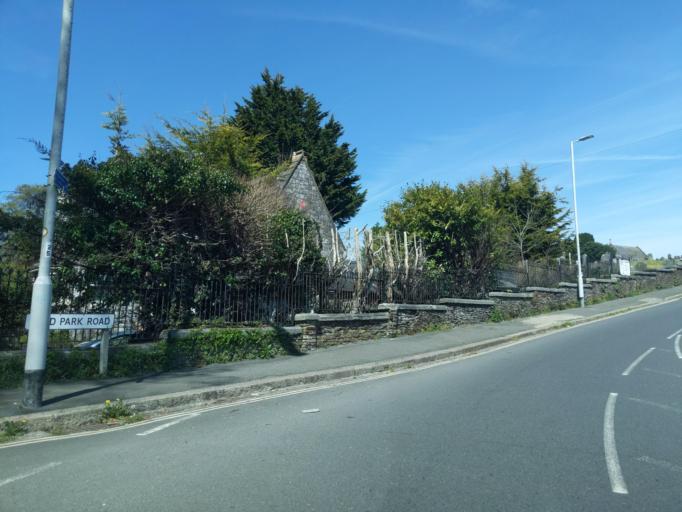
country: GB
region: England
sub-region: Plymouth
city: Plymouth
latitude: 50.3812
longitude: -4.1446
